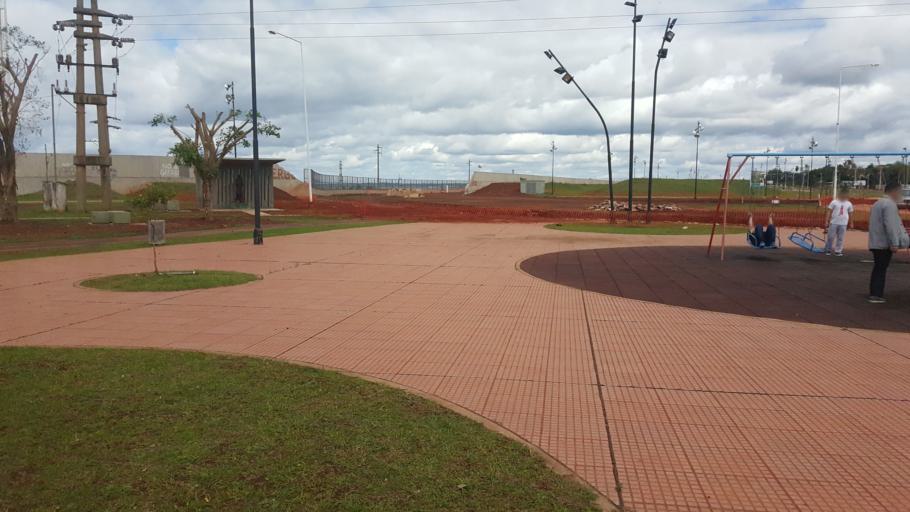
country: AR
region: Misiones
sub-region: Departamento de Capital
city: Posadas
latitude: -27.3752
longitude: -55.8846
